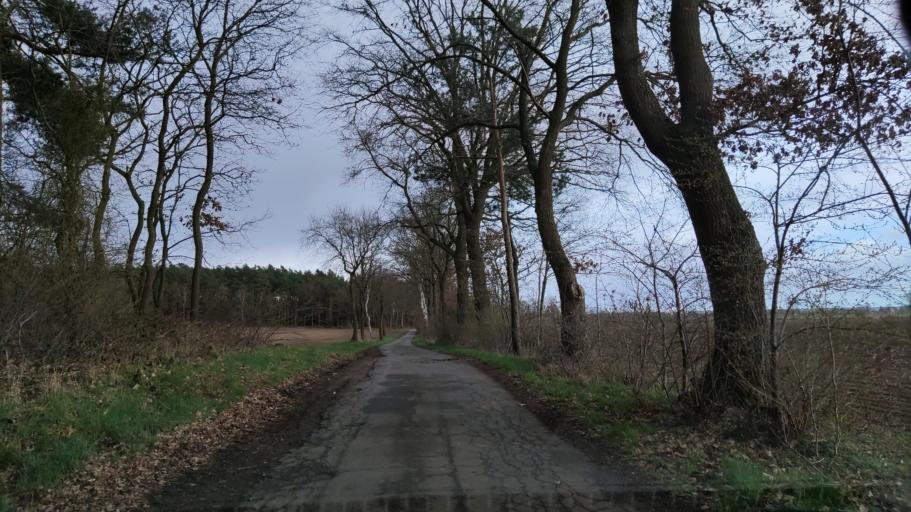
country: DE
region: Lower Saxony
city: Thomasburg
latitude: 53.1987
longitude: 10.6911
